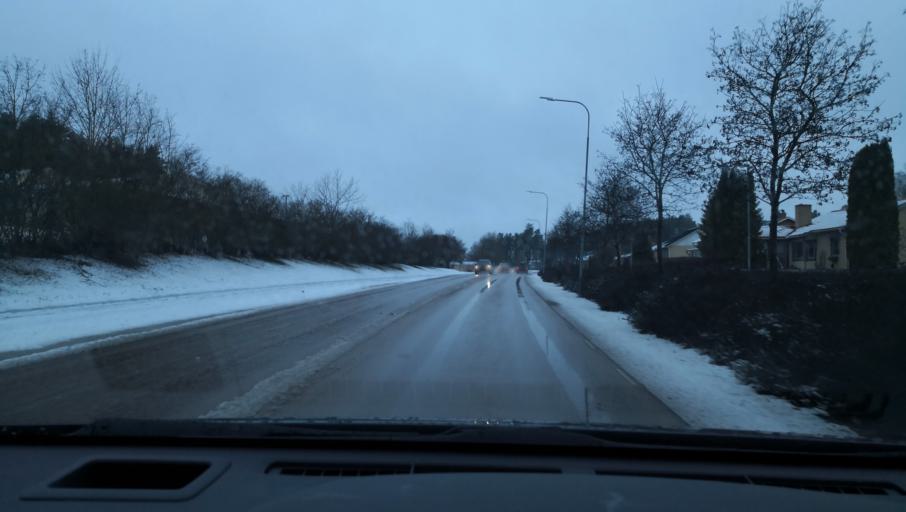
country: SE
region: Vaestmanland
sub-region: Kopings Kommun
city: Koping
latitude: 59.5206
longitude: 16.0050
